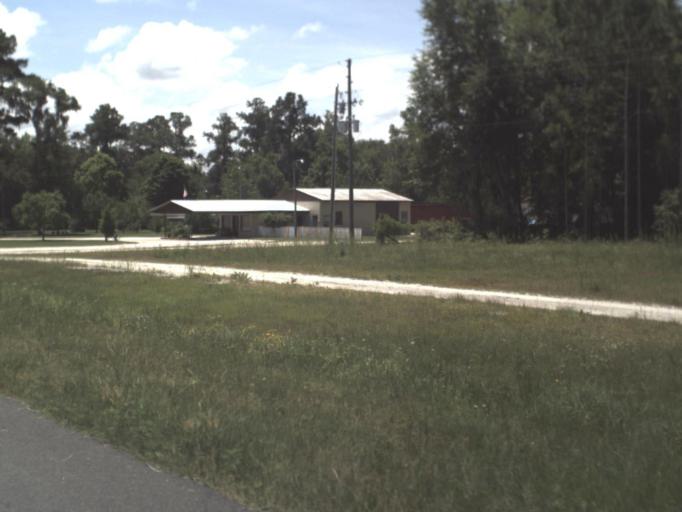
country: US
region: Florida
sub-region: Suwannee County
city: Wellborn
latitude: 30.3481
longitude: -82.7707
